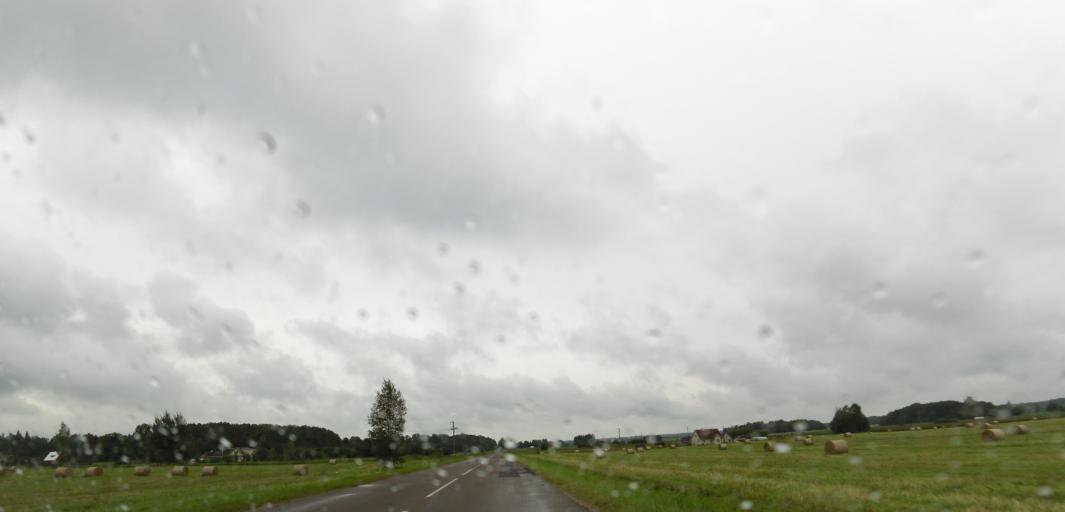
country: LT
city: Sirvintos
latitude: 55.0770
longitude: 24.9712
